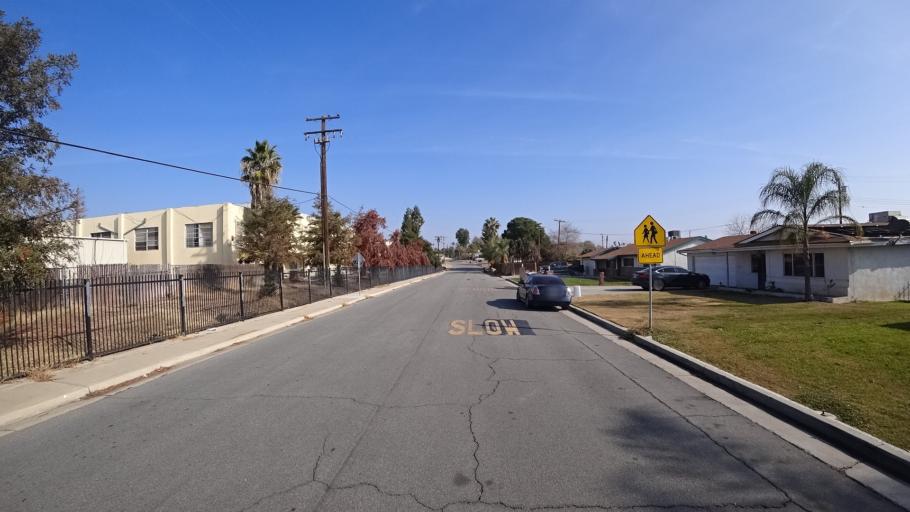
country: US
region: California
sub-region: Kern County
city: Bakersfield
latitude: 35.3903
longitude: -118.9577
